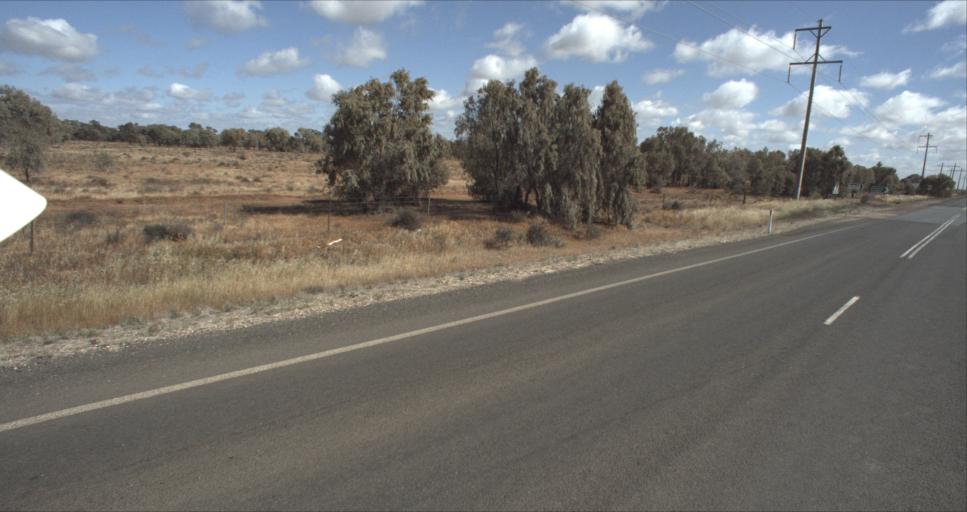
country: AU
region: New South Wales
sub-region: Murrumbidgee Shire
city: Darlington Point
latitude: -34.5177
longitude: 146.1763
